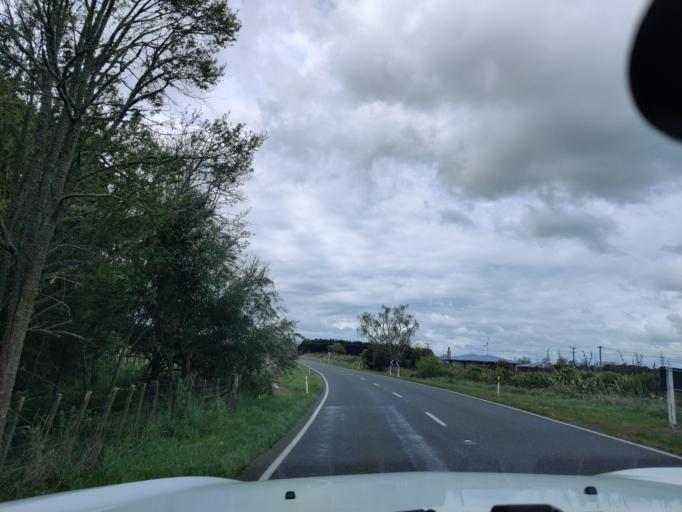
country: NZ
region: Manawatu-Wanganui
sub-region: Palmerston North City
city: Palmerston North
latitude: -40.2466
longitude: 175.5412
